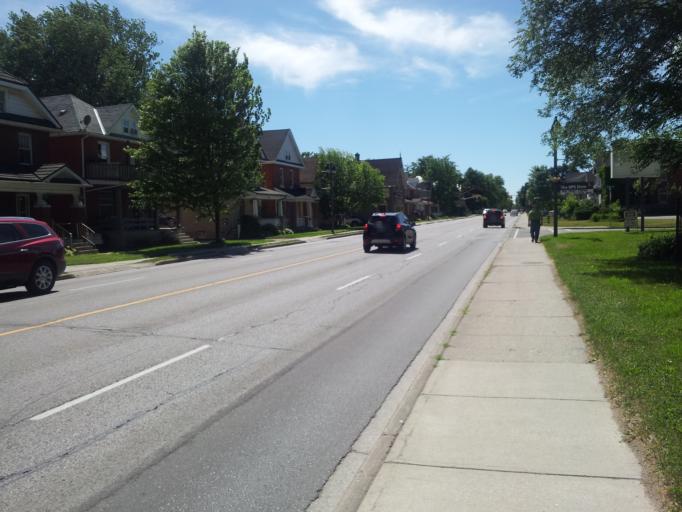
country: CA
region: Ontario
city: Stratford
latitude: 43.3713
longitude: -80.9706
